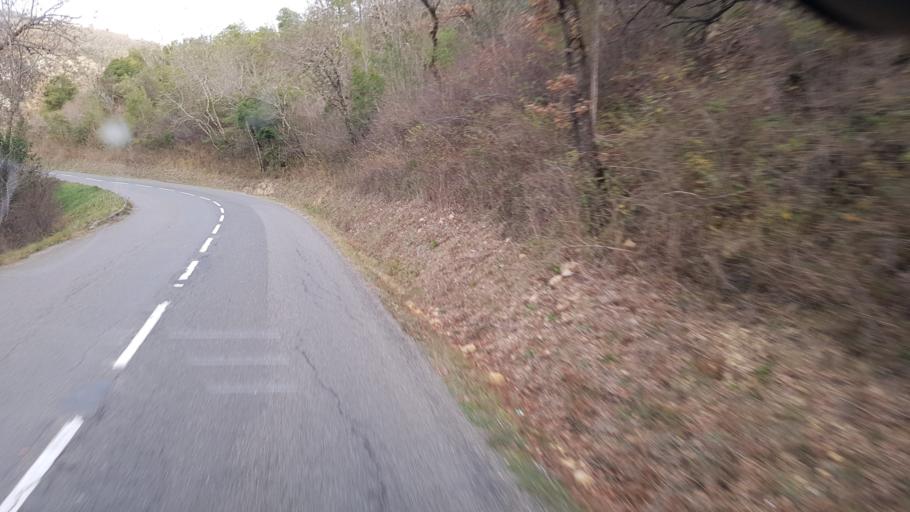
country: FR
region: Midi-Pyrenees
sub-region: Departement du Tarn-et-Garonne
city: Montricoux
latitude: 44.0188
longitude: 1.6772
